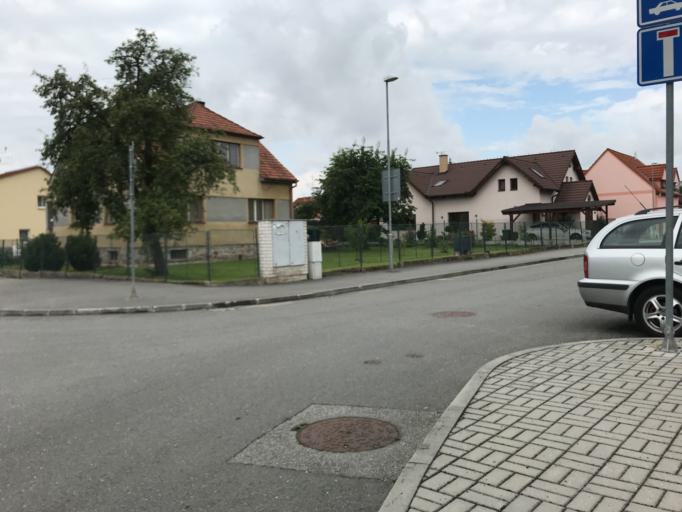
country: CZ
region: Jihocesky
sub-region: Okres Jindrichuv Hradec
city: Trebon
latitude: 49.0070
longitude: 14.7560
